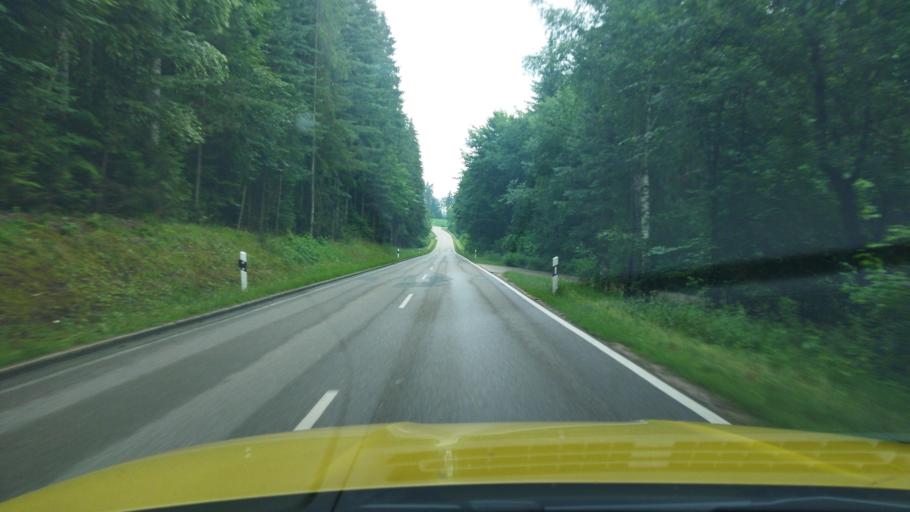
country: DE
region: Bavaria
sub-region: Regierungsbezirk Mittelfranken
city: Pleinfeld
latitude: 49.0914
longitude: 11.0032
